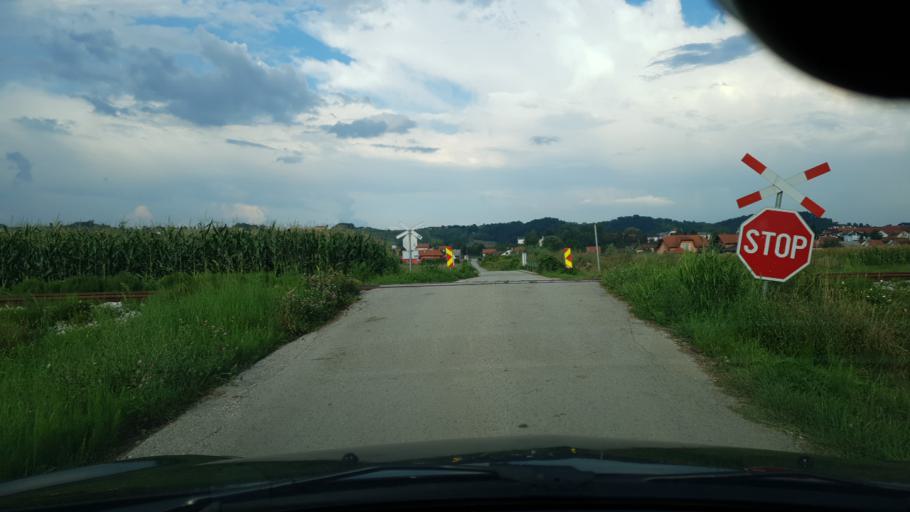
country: HR
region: Krapinsko-Zagorska
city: Zabok
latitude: 46.0841
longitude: 15.8983
